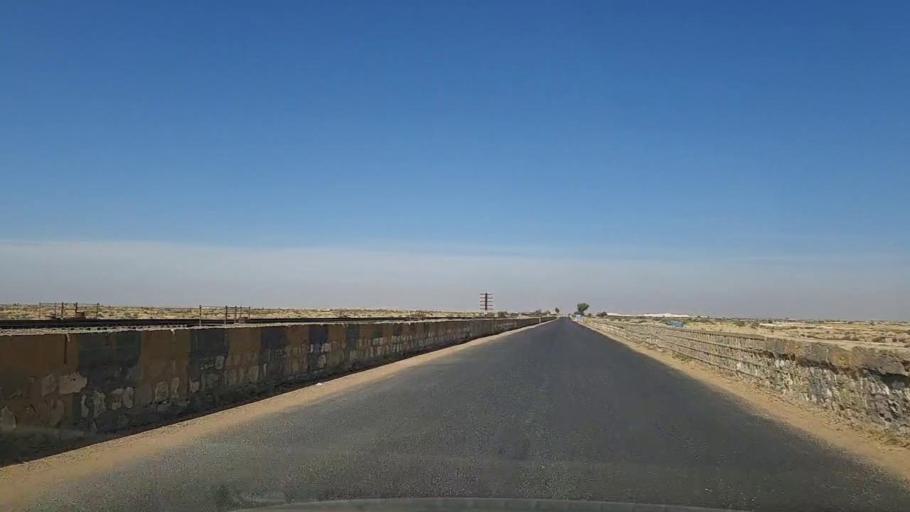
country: PK
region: Sindh
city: Kotri
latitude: 25.2980
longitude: 68.2036
